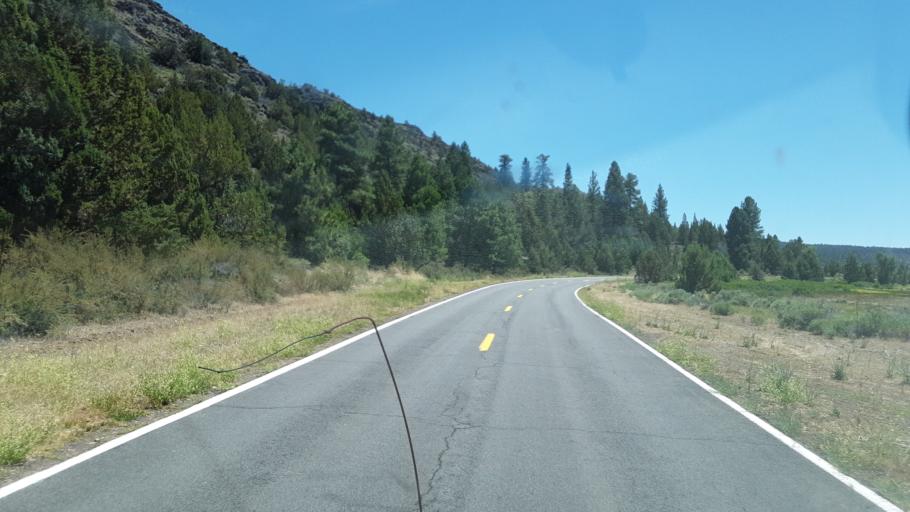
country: US
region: California
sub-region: Lassen County
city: Susanville
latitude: 40.6695
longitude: -120.6567
